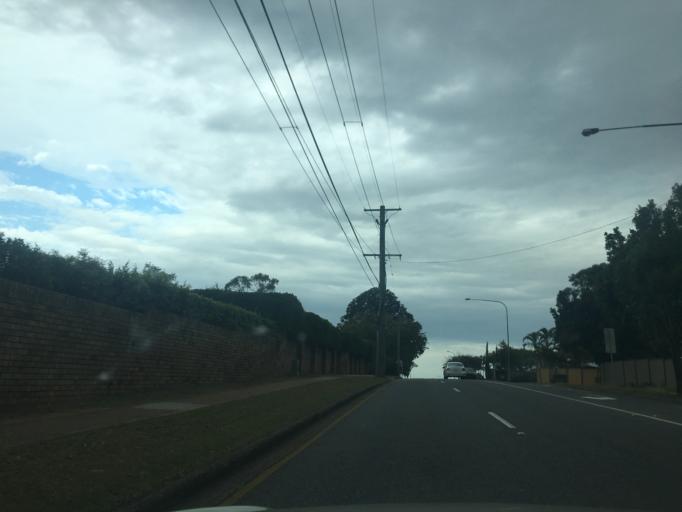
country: AU
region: Queensland
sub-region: Brisbane
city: Bridegman Downs
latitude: -27.3466
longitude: 153.0162
